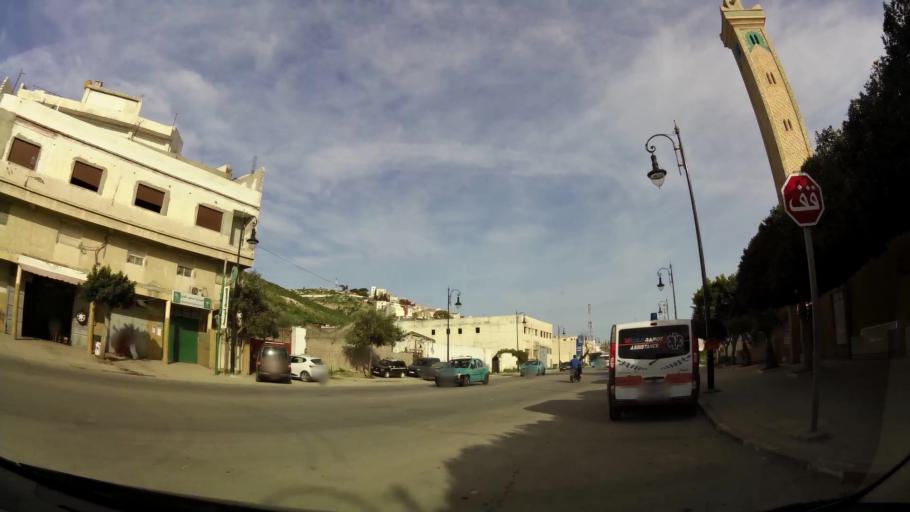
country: MA
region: Tanger-Tetouan
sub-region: Tanger-Assilah
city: Tangier
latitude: 35.7645
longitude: -5.7831
